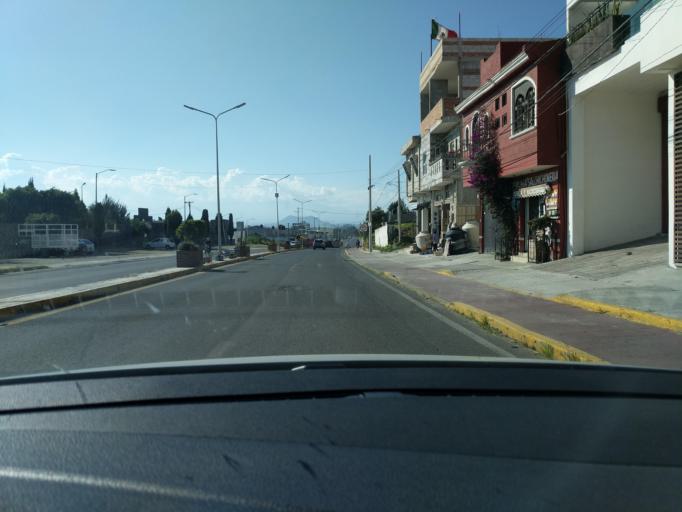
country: MX
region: Puebla
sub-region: San Gregorio Atzompa
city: Chipilo de Francisco Javier Mina
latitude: 19.0232
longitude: -98.3099
